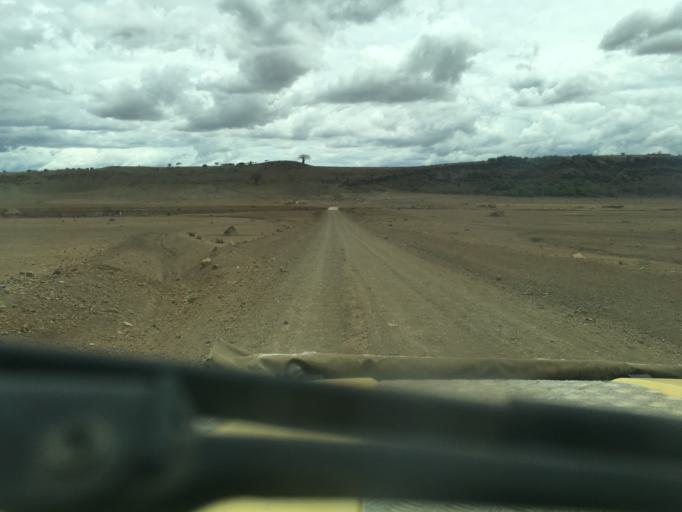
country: TZ
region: Arusha
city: Mto wa Mbu
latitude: -3.2128
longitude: 35.9522
